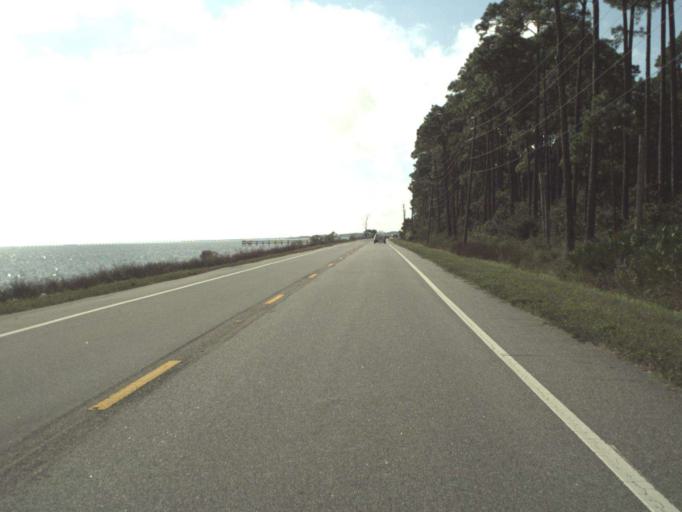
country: US
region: Florida
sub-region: Franklin County
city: Eastpoint
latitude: 29.7603
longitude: -84.8205
